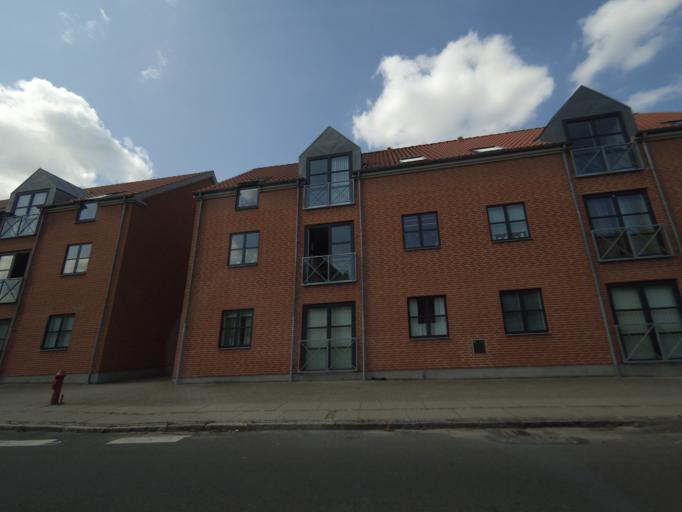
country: DK
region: South Denmark
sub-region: Assens Kommune
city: Arup
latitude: 55.3759
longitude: 10.0462
